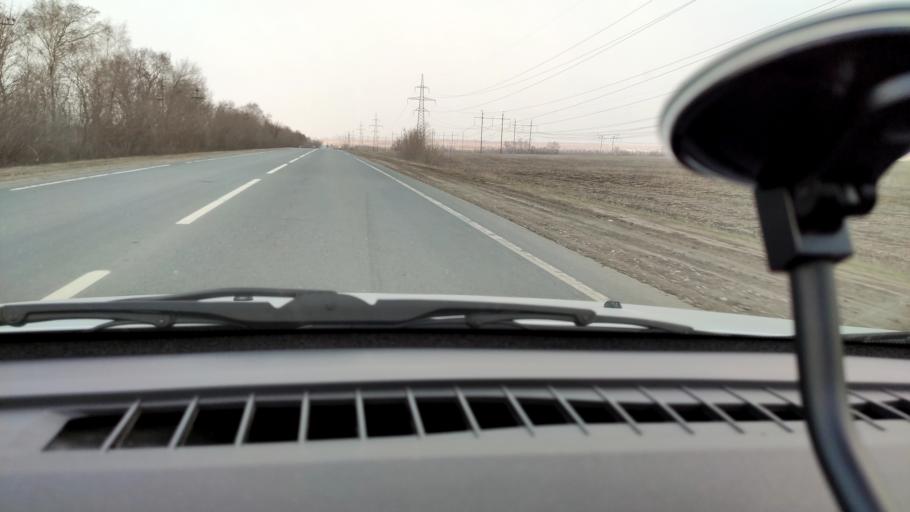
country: RU
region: Samara
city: Dubovyy Umet
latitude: 53.0768
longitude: 50.3869
